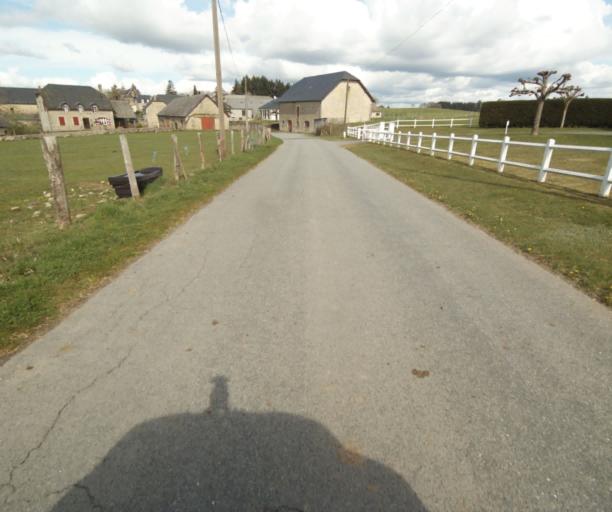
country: FR
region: Limousin
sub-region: Departement de la Correze
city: Correze
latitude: 45.3524
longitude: 1.8867
